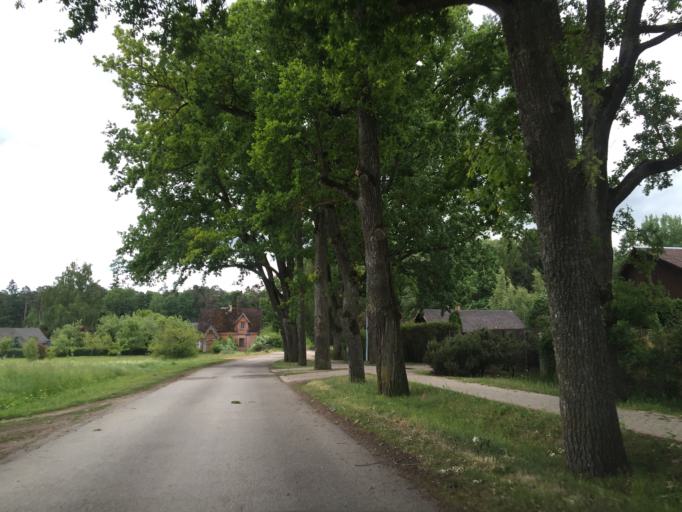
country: LV
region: Lecava
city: Iecava
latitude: 56.5894
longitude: 24.2033
